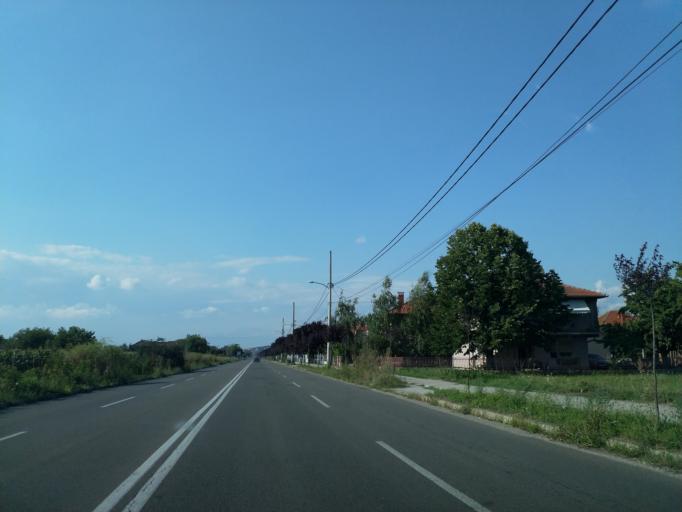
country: RS
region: Central Serbia
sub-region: Pomoravski Okrug
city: Paracin
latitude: 43.8385
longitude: 21.4155
